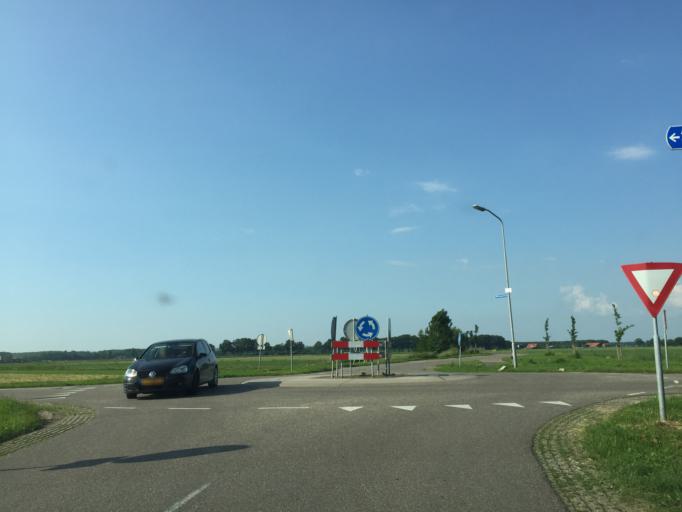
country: NL
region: North Brabant
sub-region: Gemeente Oss
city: Oss
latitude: 51.8401
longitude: 5.4997
